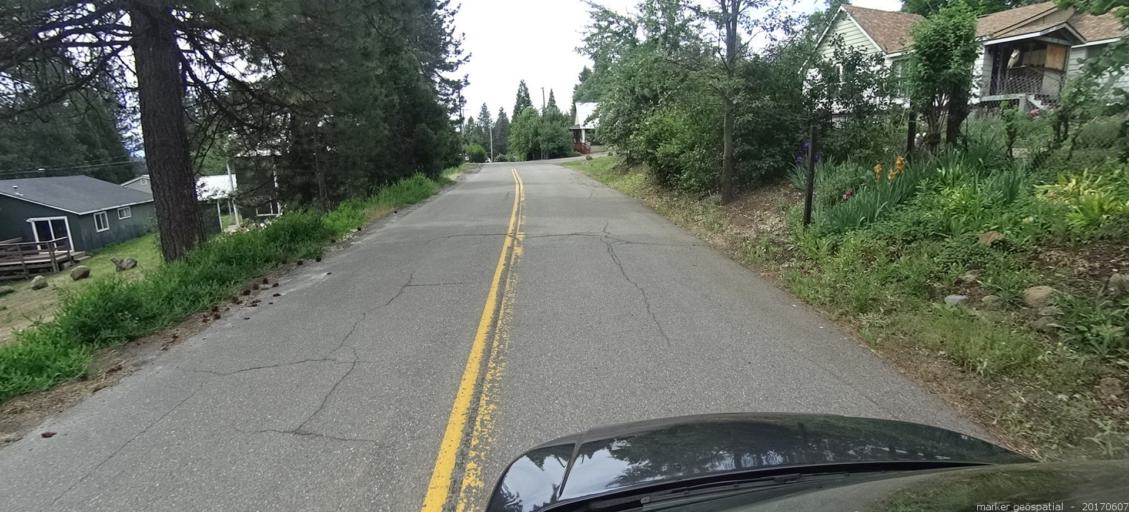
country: US
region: California
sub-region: Siskiyou County
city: McCloud
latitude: 41.2530
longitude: -122.1425
